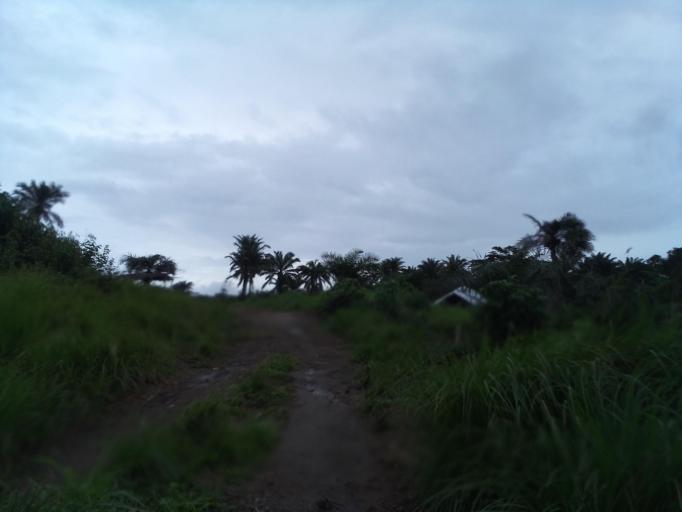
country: SL
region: Eastern Province
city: Kenema
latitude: 7.8749
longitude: -11.1562
